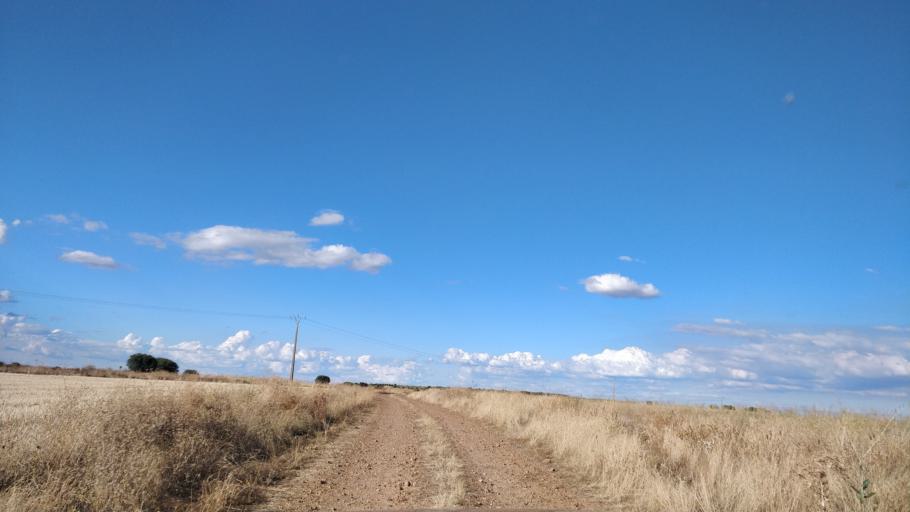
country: ES
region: Castille and Leon
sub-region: Provincia de Leon
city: Santa Cristina de Valmadrigal
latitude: 42.3391
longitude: -5.2736
